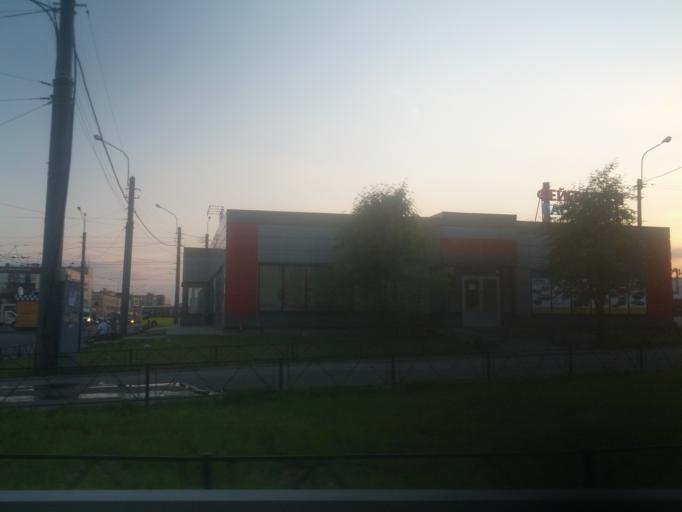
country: RU
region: St.-Petersburg
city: Staraya Derevnya
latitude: 59.9907
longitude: 30.2557
